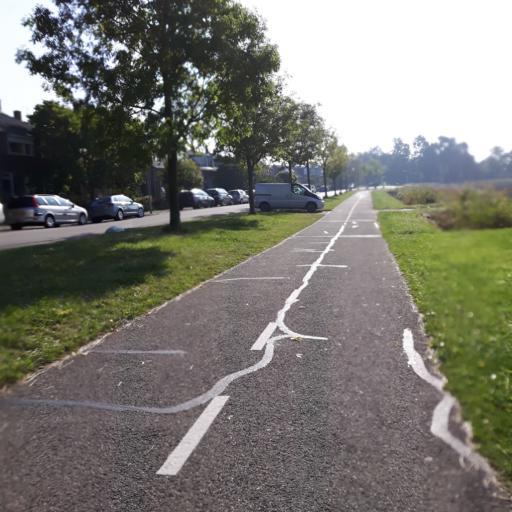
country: NL
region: Zeeland
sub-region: Gemeente Goes
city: Goes
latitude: 51.4956
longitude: 3.9187
